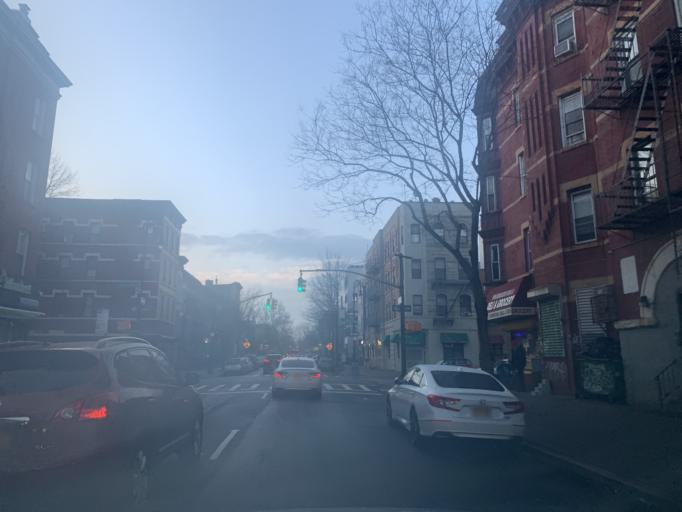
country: US
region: New York
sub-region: Kings County
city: Brooklyn
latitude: 40.6908
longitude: -73.9336
